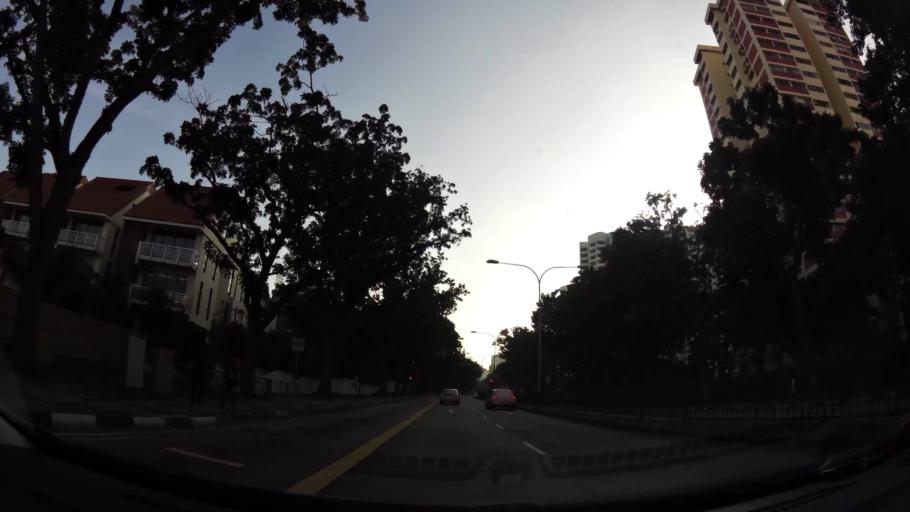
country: SG
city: Singapore
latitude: 1.3082
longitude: 103.9220
